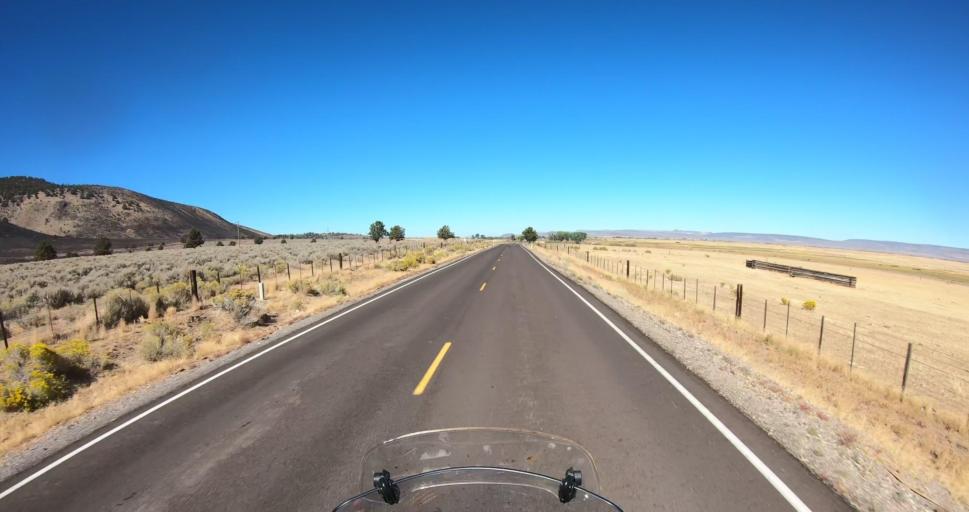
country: US
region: Oregon
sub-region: Lake County
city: Lakeview
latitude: 42.6491
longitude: -120.5217
